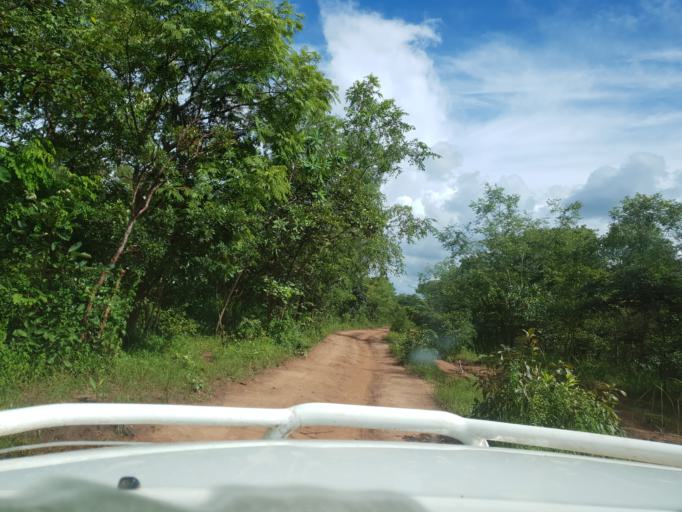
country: CI
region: Savanes
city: Tengrela
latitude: 10.4653
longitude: -6.7978
